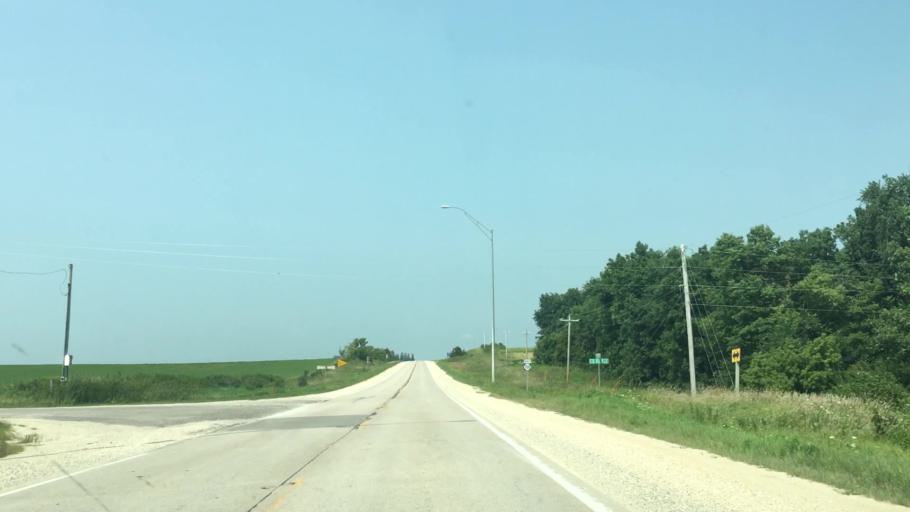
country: US
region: Iowa
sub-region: Fayette County
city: West Union
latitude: 43.1289
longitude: -91.8691
